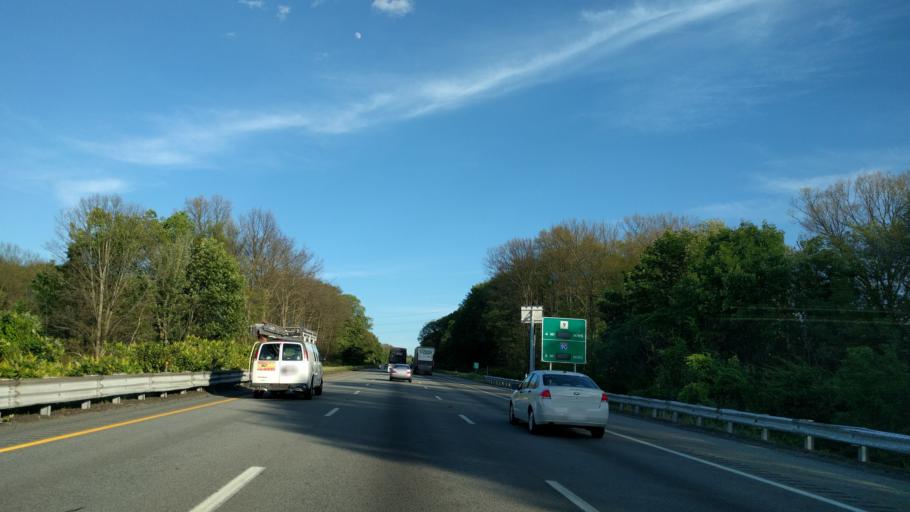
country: US
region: Massachusetts
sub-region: Middlesex County
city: Marlborough
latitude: 42.3557
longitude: -71.5828
